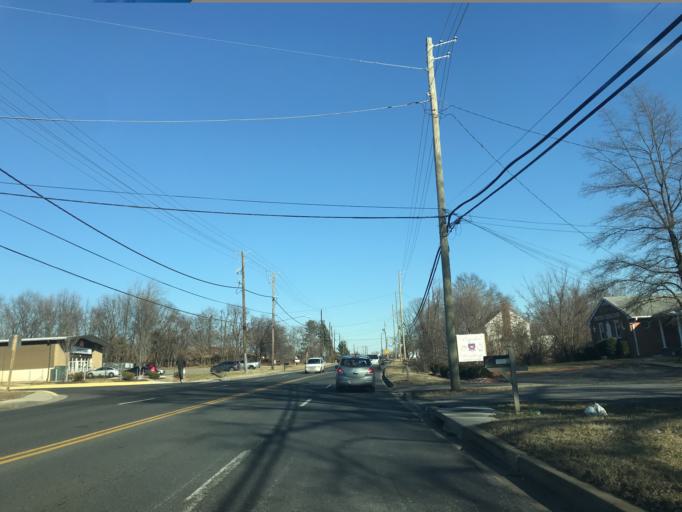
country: US
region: Maryland
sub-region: Prince George's County
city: Clinton
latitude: 38.7661
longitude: -76.8950
